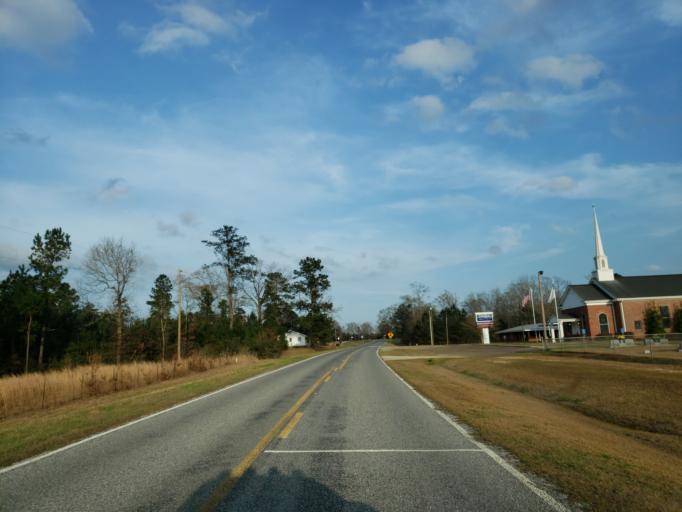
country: US
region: Mississippi
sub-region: Clarke County
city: Stonewall
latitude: 32.1734
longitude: -88.6825
